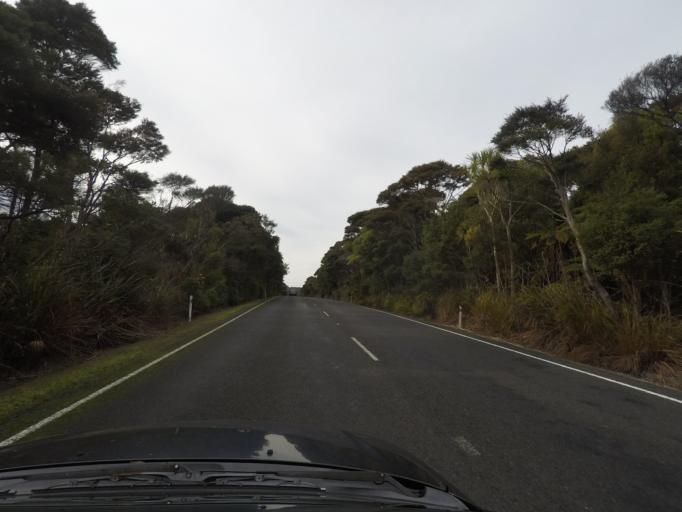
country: NZ
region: Auckland
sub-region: Auckland
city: Titirangi
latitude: -36.9435
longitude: 174.5489
